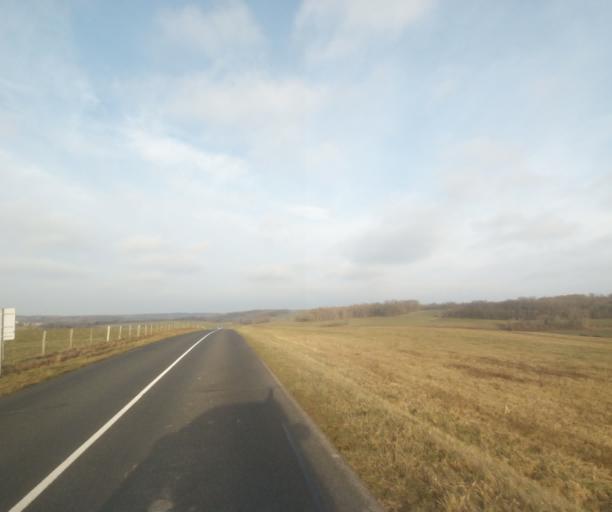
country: FR
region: Champagne-Ardenne
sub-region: Departement de la Marne
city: Sermaize-les-Bains
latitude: 48.7314
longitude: 4.9322
